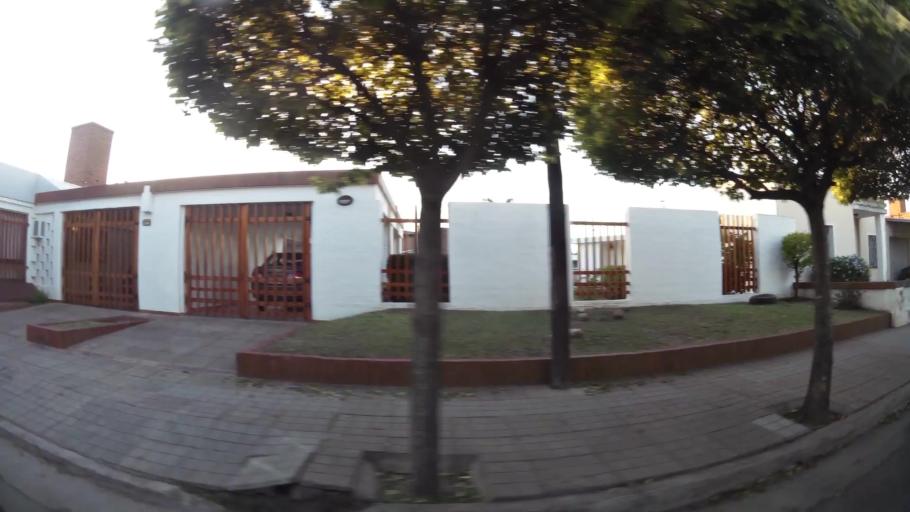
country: AR
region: Cordoba
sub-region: Departamento de Capital
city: Cordoba
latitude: -31.3751
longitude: -64.2168
